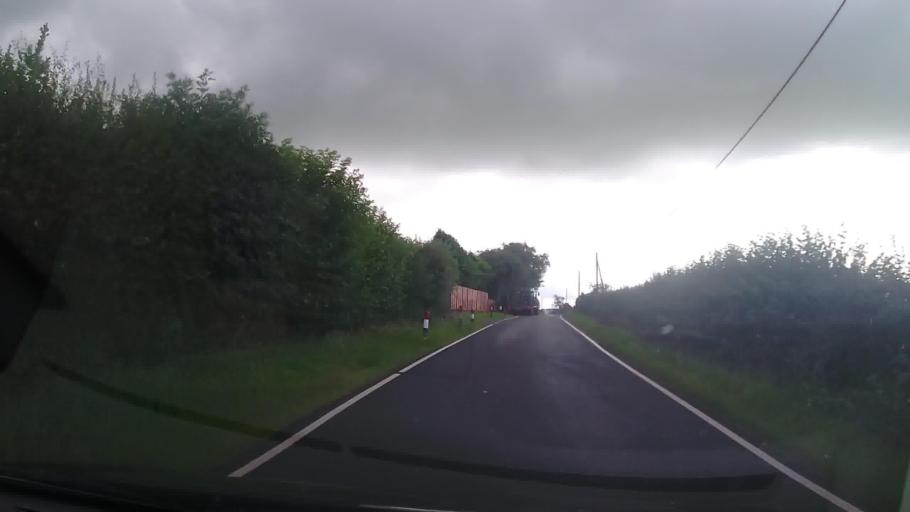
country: GB
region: England
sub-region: Shropshire
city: Norbury
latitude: 52.5865
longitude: -2.9550
